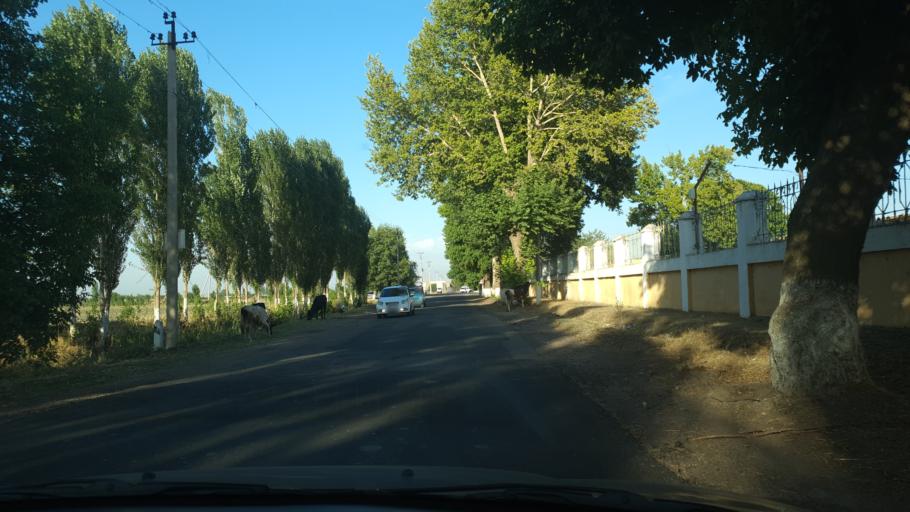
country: UZ
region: Toshkent
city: Tuytepa
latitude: 41.0855
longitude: 69.3421
